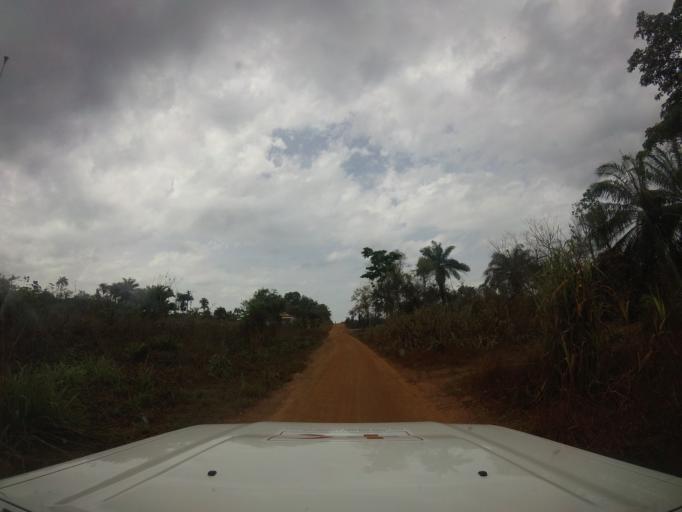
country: LR
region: Grand Cape Mount
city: Robertsport
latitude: 6.9618
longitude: -11.3169
